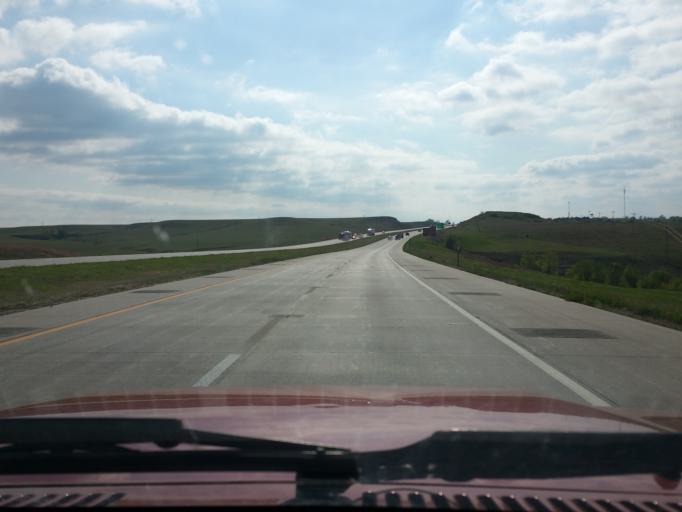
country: US
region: Kansas
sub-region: Riley County
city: Manhattan
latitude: 39.0634
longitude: -96.5179
